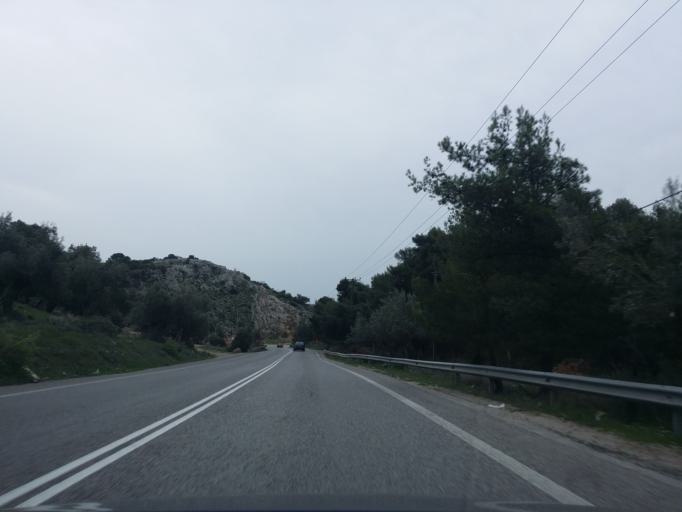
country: GR
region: Attica
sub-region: Nomarchia Dytikis Attikis
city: Mandra
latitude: 38.0933
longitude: 23.4744
